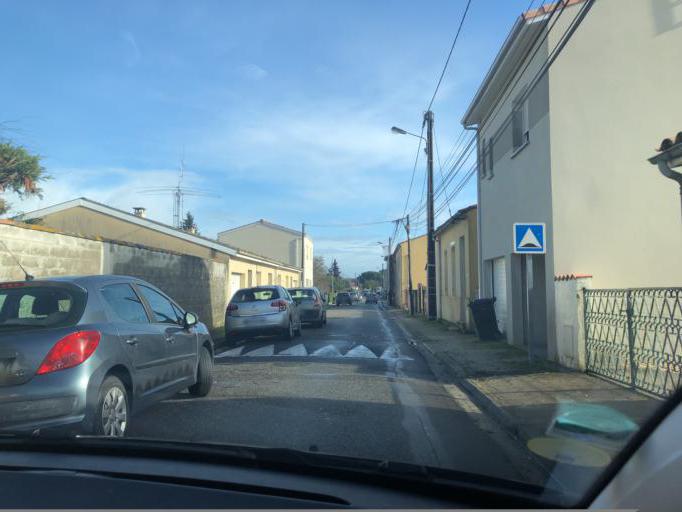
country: FR
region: Aquitaine
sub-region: Departement de la Gironde
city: Castelnau-de-Medoc
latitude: 45.0288
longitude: -0.7962
